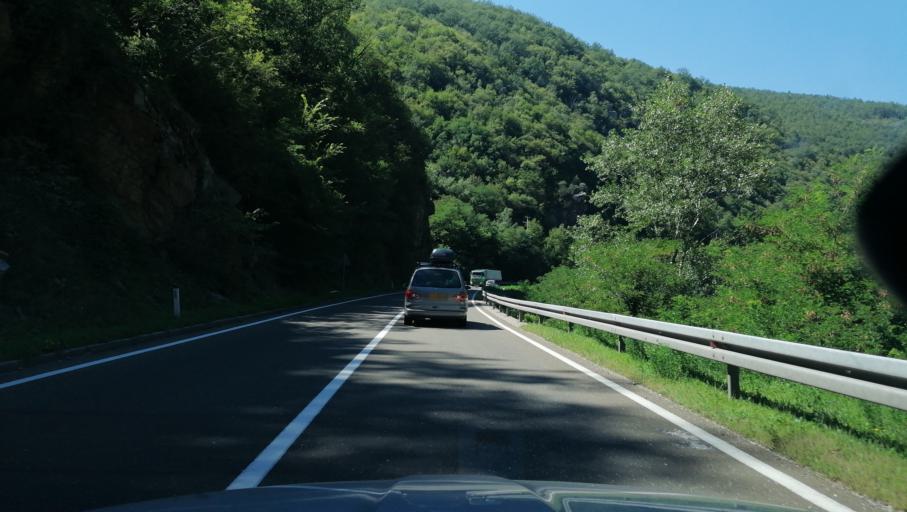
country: RS
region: Central Serbia
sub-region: Raski Okrug
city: Raska
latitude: 43.5054
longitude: 20.6158
